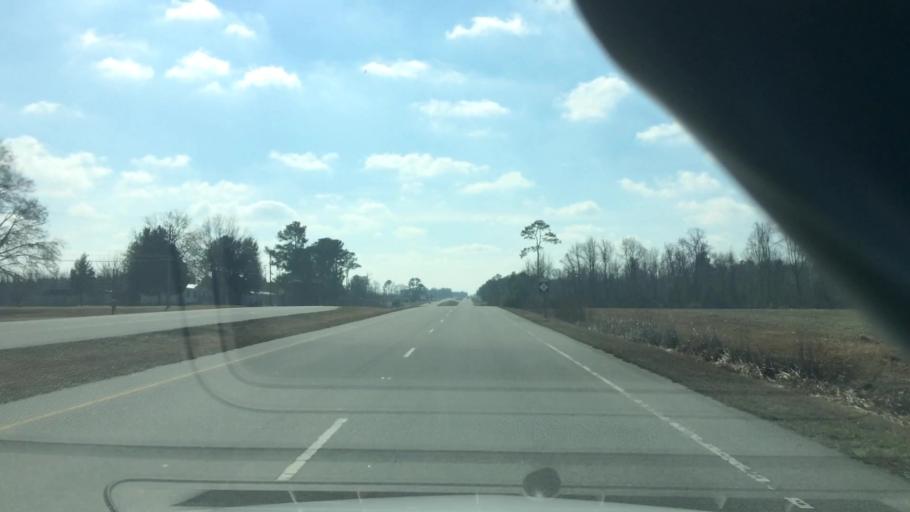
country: US
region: North Carolina
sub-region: Duplin County
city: Beulaville
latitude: 35.1098
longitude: -77.7194
